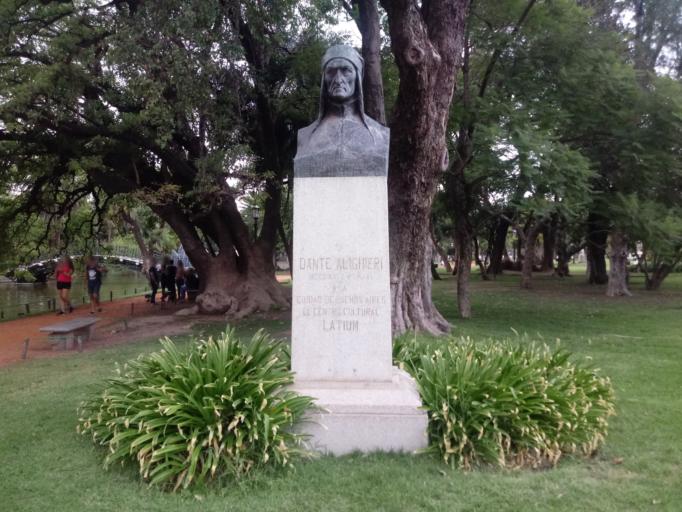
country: AR
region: Buenos Aires F.D.
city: Colegiales
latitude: -34.5710
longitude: -58.4164
